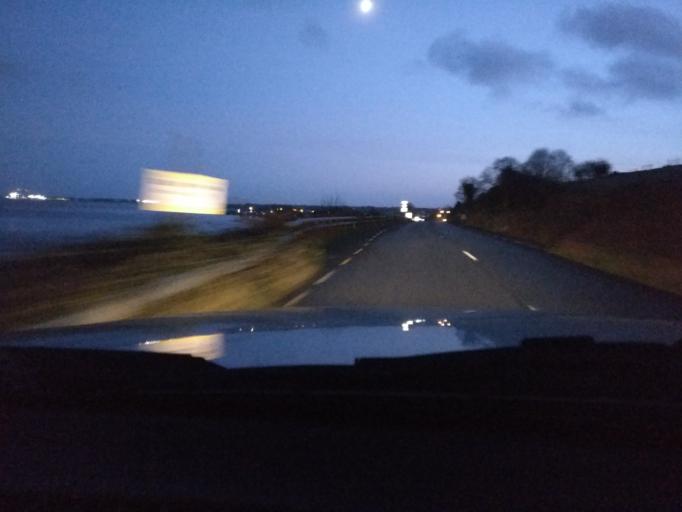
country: IE
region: Leinster
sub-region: Lu
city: Carlingford
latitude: 54.0498
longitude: -6.1925
